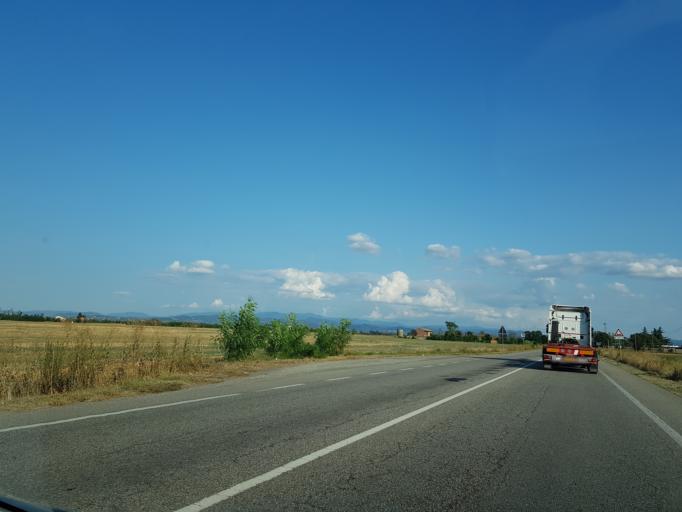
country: IT
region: Piedmont
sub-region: Provincia di Alessandria
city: Mandrogne
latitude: 44.8260
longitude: 8.7464
